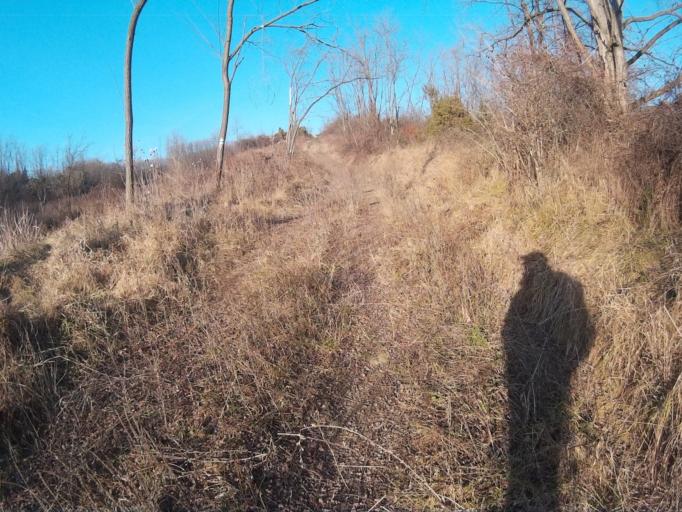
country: HU
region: Nograd
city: Bercel
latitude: 47.9584
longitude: 19.4403
